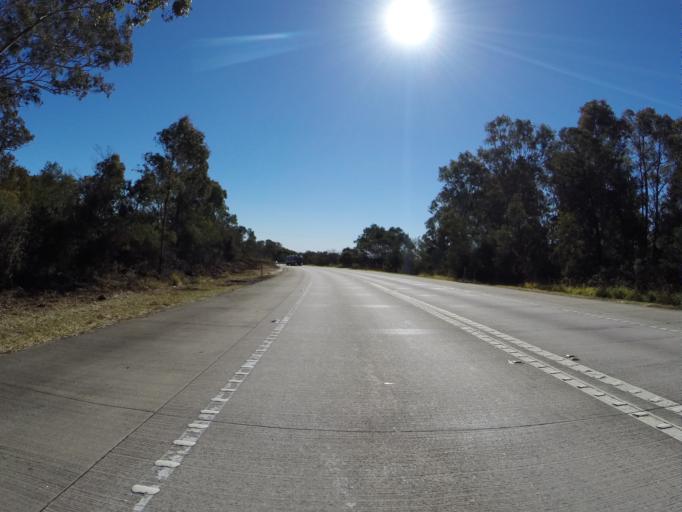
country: AU
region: New South Wales
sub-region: Wollondilly
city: Douglas Park
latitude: -34.2656
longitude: 150.7147
